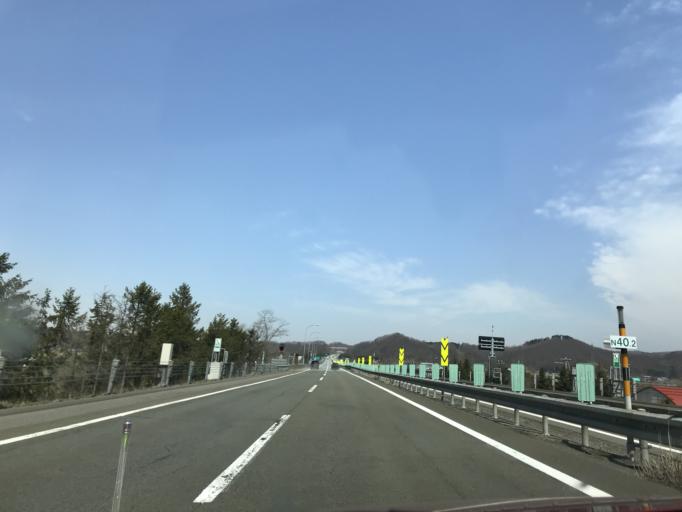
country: JP
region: Hokkaido
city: Iwamizawa
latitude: 43.2295
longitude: 141.8305
